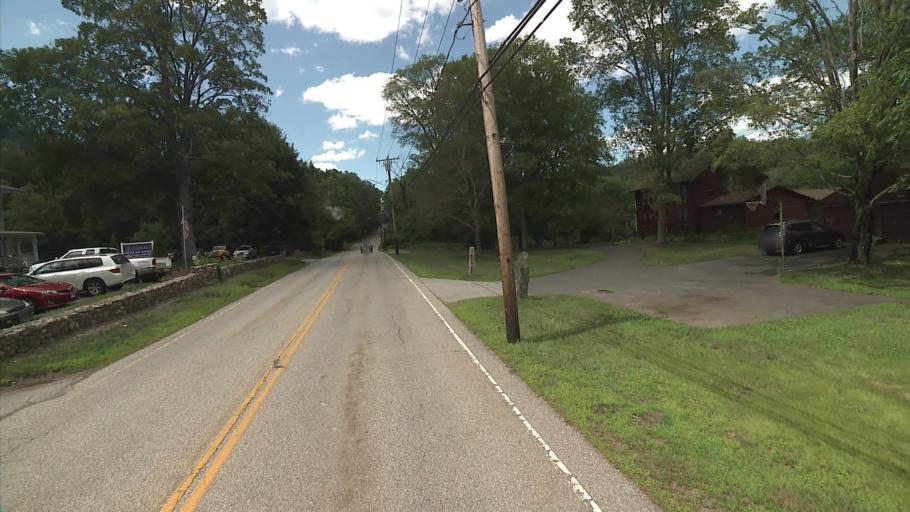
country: US
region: Connecticut
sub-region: Middlesex County
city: East Hampton
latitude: 41.5585
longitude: -72.5539
